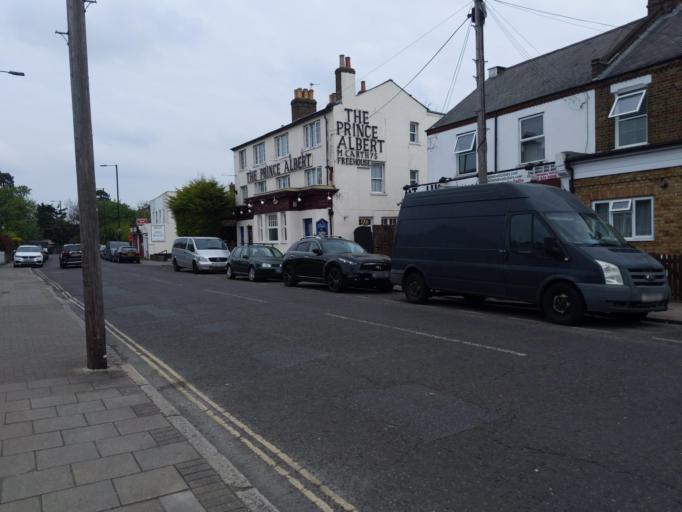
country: GB
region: England
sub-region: Greater London
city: Hounslow
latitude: 51.4544
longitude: -0.3587
